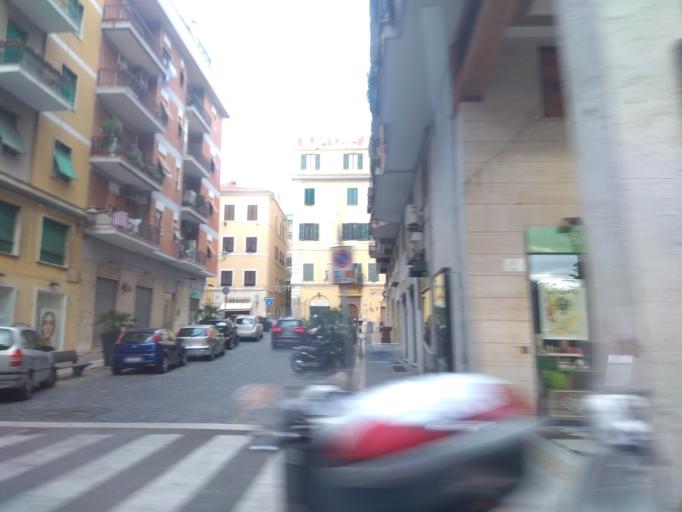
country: IT
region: Latium
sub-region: Citta metropolitana di Roma Capitale
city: Civitavecchia
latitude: 42.0933
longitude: 11.7910
